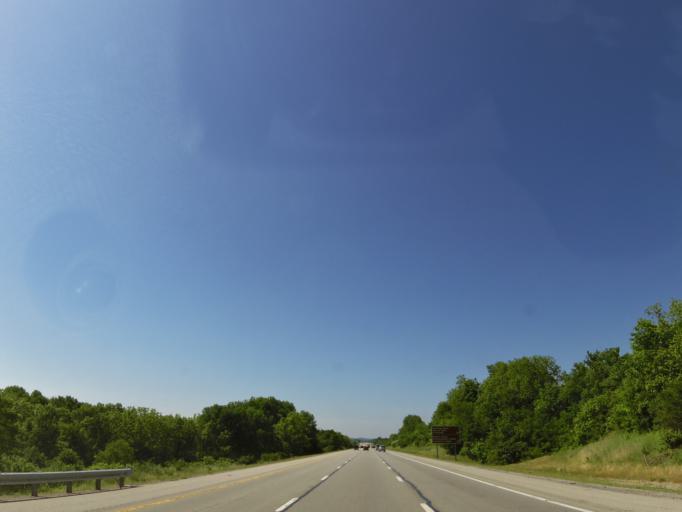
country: US
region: Kentucky
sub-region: Madison County
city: Berea
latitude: 37.6581
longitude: -84.3126
